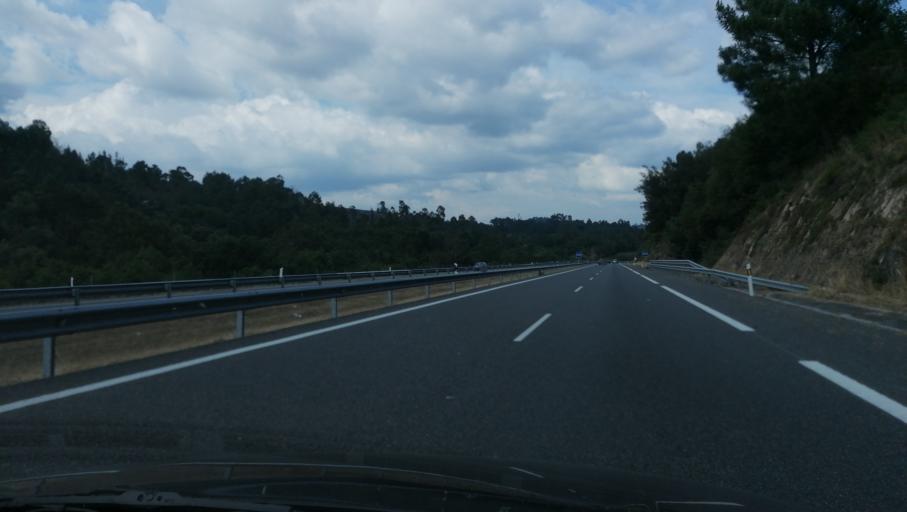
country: ES
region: Galicia
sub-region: Provincia de Ourense
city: Carballeda de Avia
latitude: 42.3055
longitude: -8.1770
